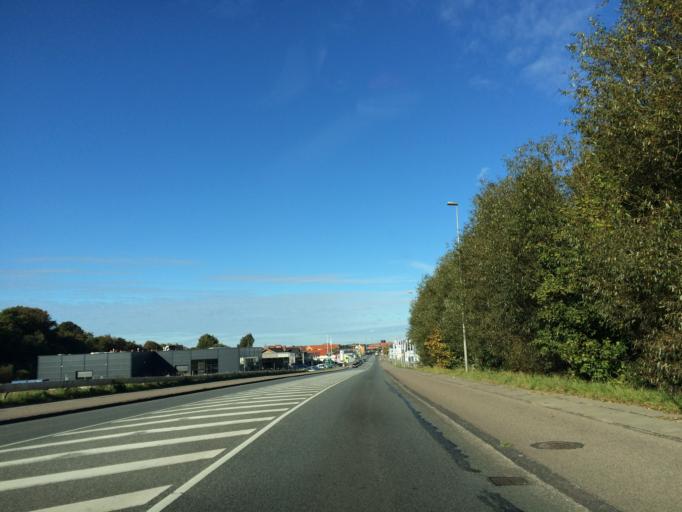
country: DK
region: Central Jutland
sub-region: Randers Kommune
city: Randers
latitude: 56.4510
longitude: 10.0546
